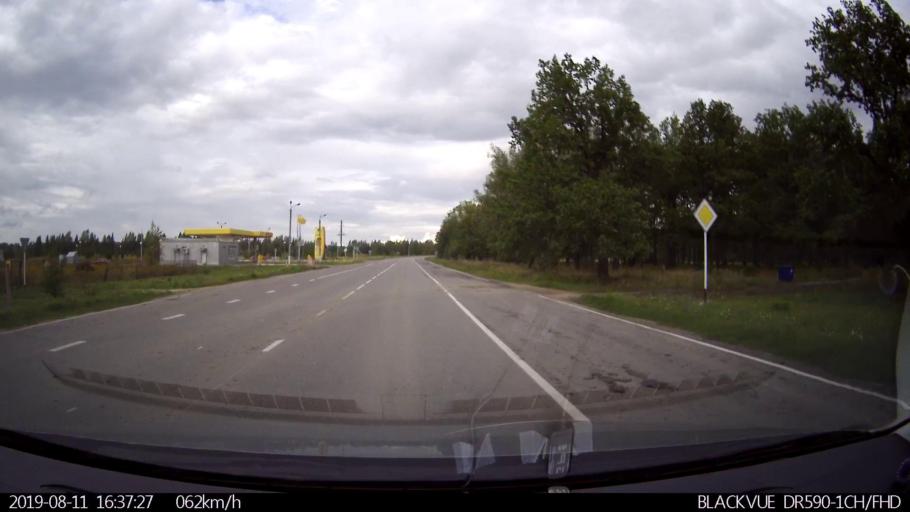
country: RU
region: Ulyanovsk
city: Mayna
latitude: 54.1274
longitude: 47.6144
